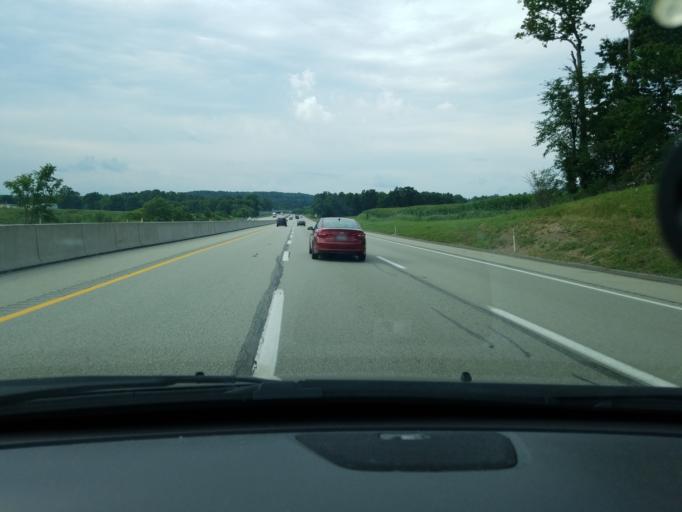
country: US
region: Pennsylvania
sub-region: Lawrence County
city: New Beaver
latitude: 40.8549
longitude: -80.3968
